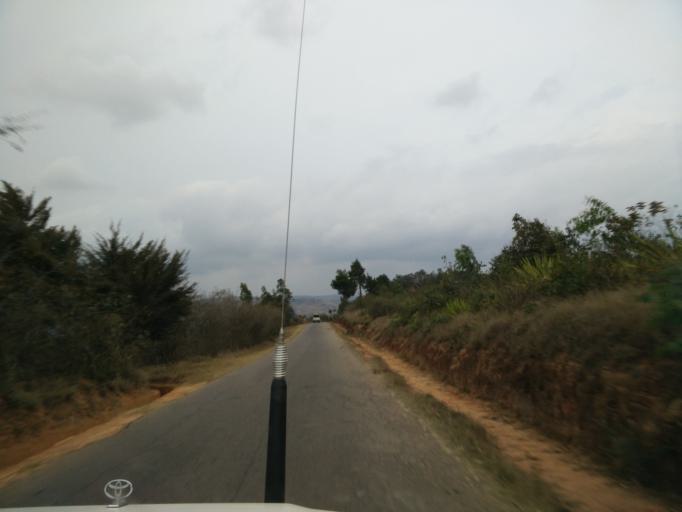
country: MG
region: Upper Matsiatra
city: Fianarantsoa
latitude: -21.5372
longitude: 47.0480
